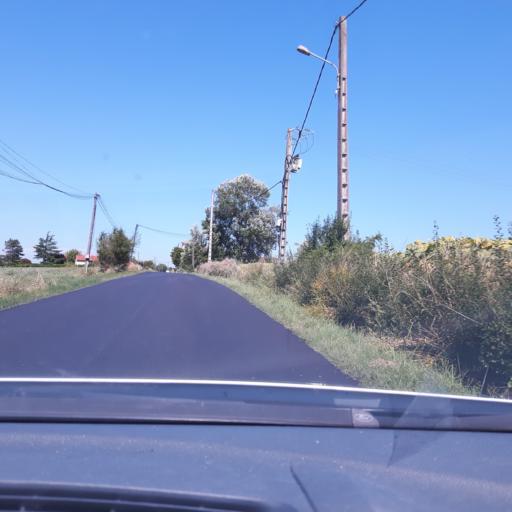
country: FR
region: Midi-Pyrenees
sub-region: Departement de la Haute-Garonne
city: Bouloc
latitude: 43.7840
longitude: 1.3990
